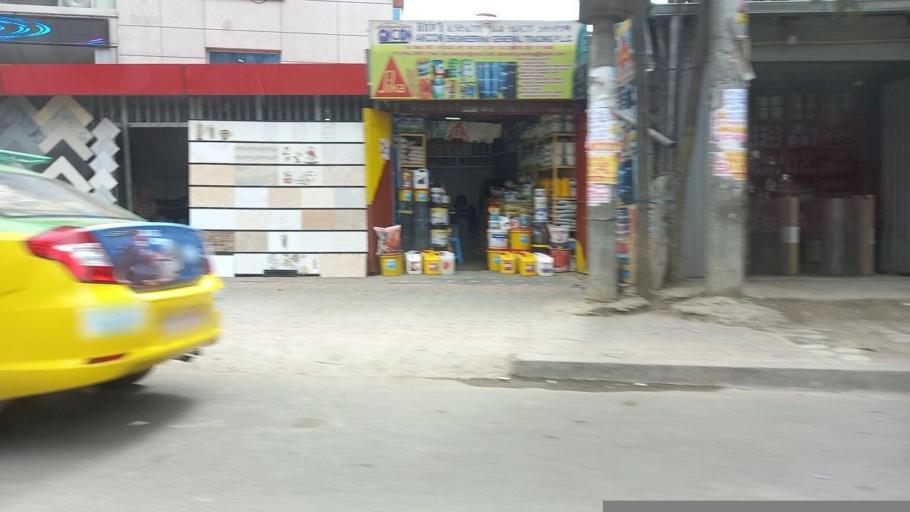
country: ET
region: Adis Abeba
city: Addis Ababa
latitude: 9.0222
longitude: 38.7866
